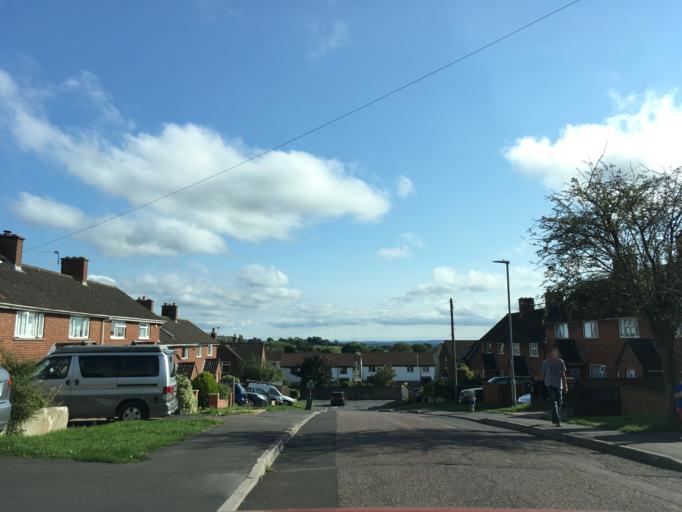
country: GB
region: England
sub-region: Somerset
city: Wells
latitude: 51.2073
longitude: -2.6622
